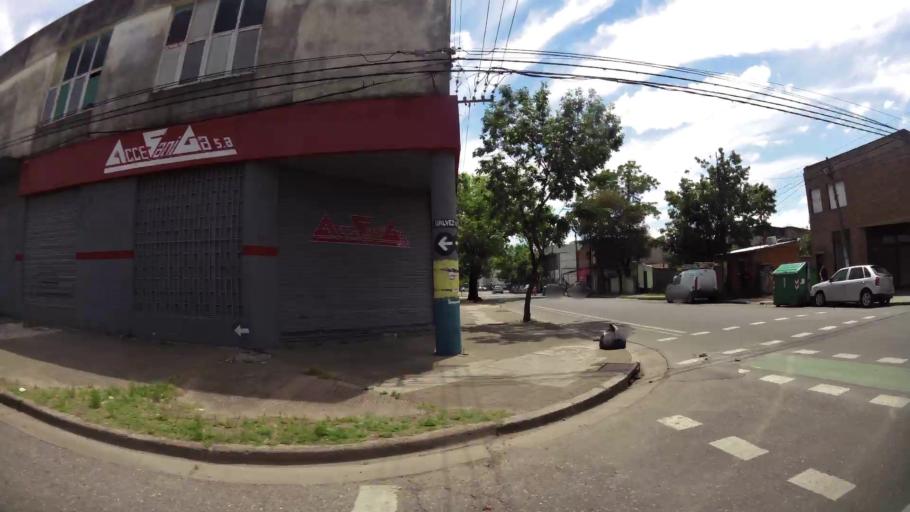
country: AR
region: Santa Fe
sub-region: Departamento de Rosario
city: Rosario
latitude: -32.9712
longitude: -60.6299
